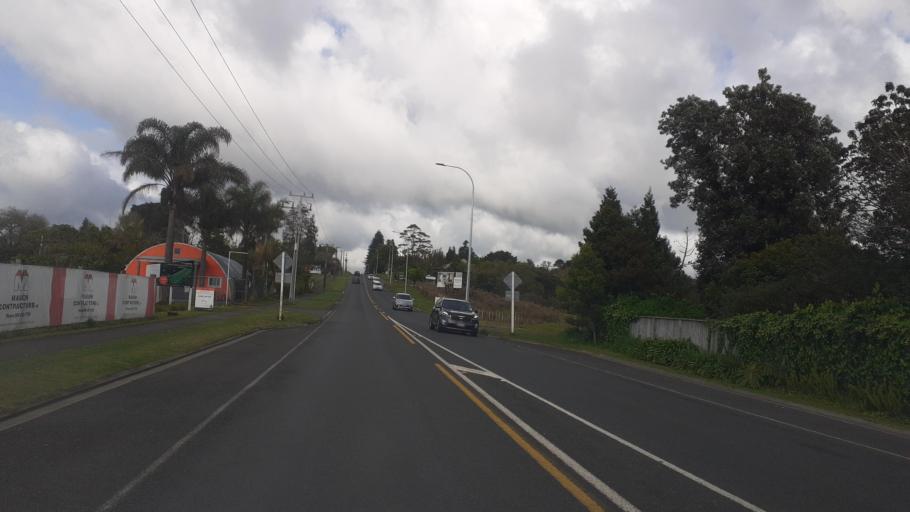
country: NZ
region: Northland
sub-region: Far North District
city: Kerikeri
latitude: -35.2352
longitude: 173.9423
